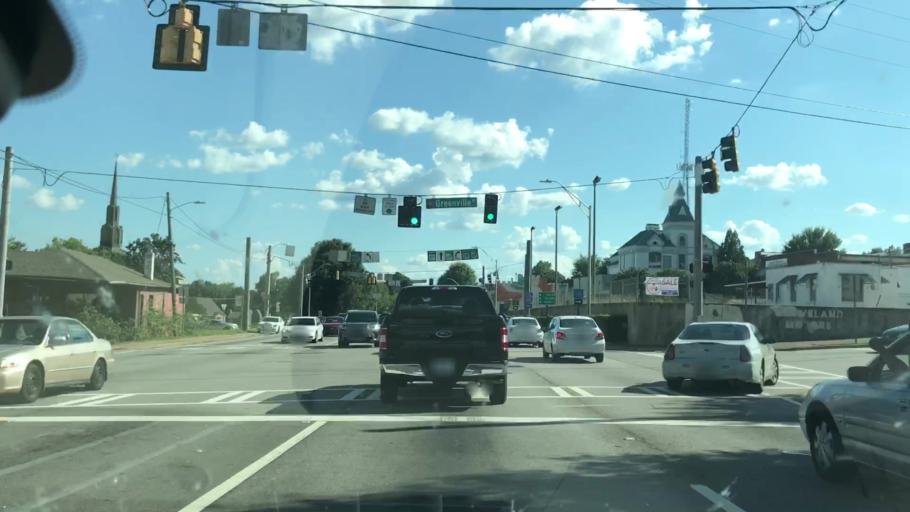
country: US
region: Georgia
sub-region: Troup County
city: La Grange
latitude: 33.0397
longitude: -85.0296
